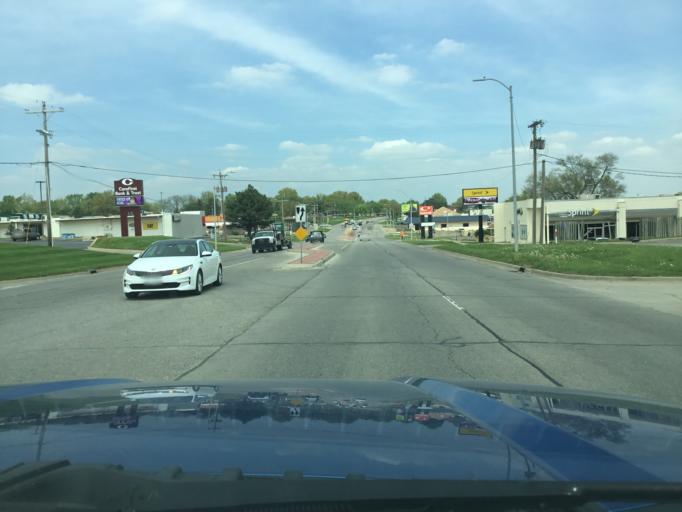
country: US
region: Kansas
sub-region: Shawnee County
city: Topeka
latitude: 39.0121
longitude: -95.6876
